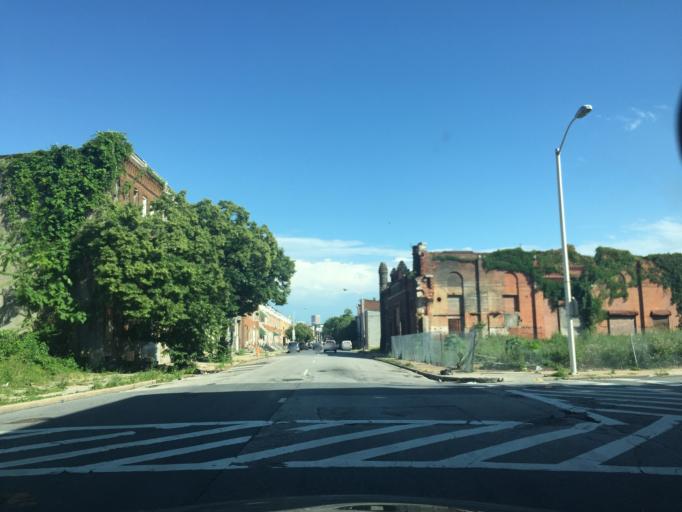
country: US
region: Maryland
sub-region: City of Baltimore
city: Baltimore
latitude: 39.3135
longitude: -76.6413
